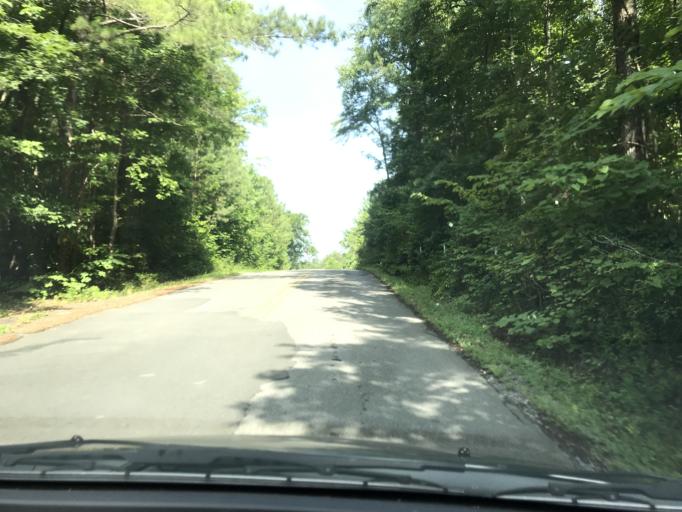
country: US
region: Tennessee
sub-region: Hamilton County
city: Apison
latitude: 35.0510
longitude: -84.9948
